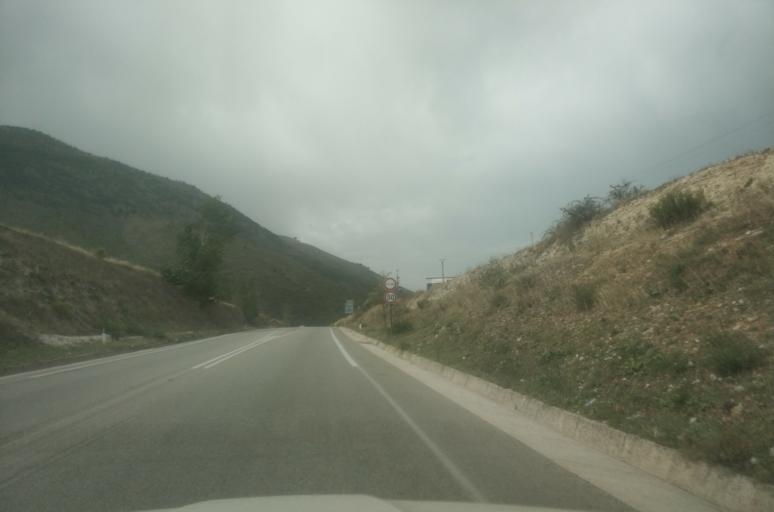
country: AL
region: Gjirokaster
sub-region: Rrethi i Tepelenes
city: Tepelene
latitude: 40.2687
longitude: 20.0464
